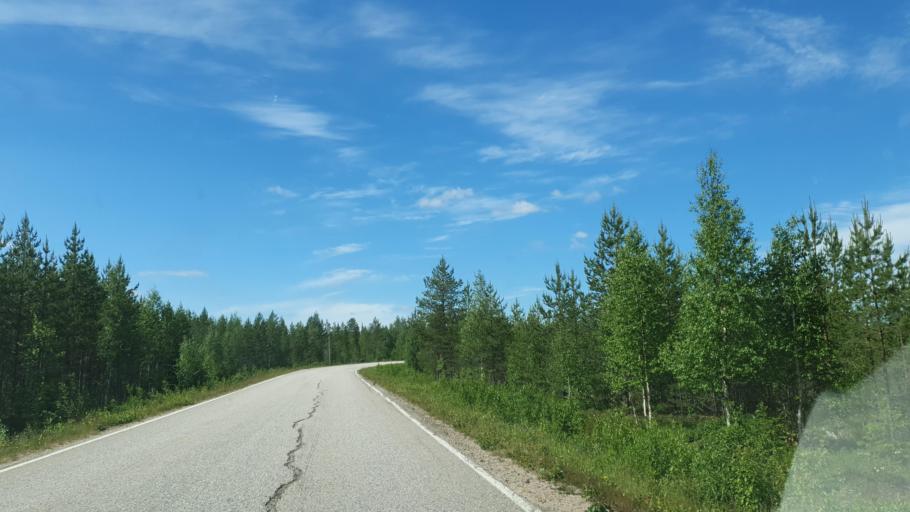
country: FI
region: Kainuu
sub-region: Kehys-Kainuu
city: Suomussalmi
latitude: 64.5740
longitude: 29.0226
